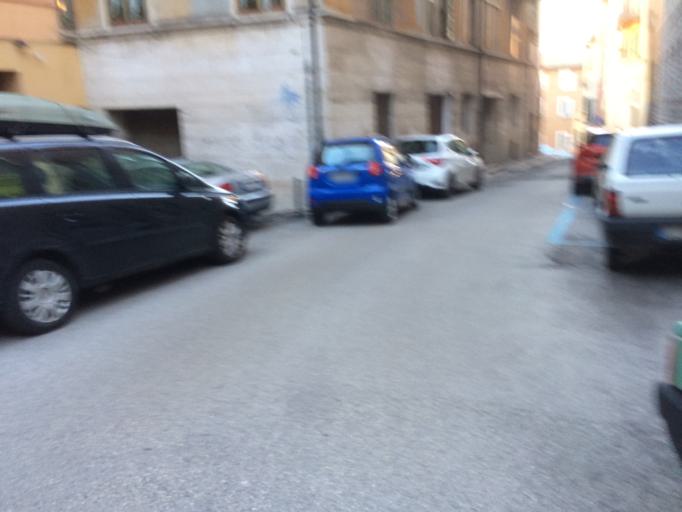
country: IT
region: Umbria
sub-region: Provincia di Perugia
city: Perugia
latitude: 43.1133
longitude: 12.3861
